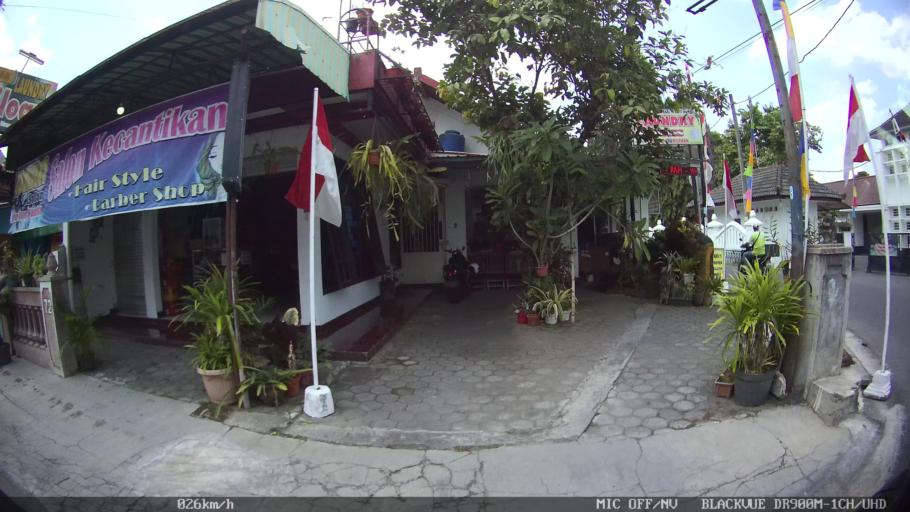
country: ID
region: Daerah Istimewa Yogyakarta
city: Gamping Lor
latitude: -7.8084
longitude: 110.3435
